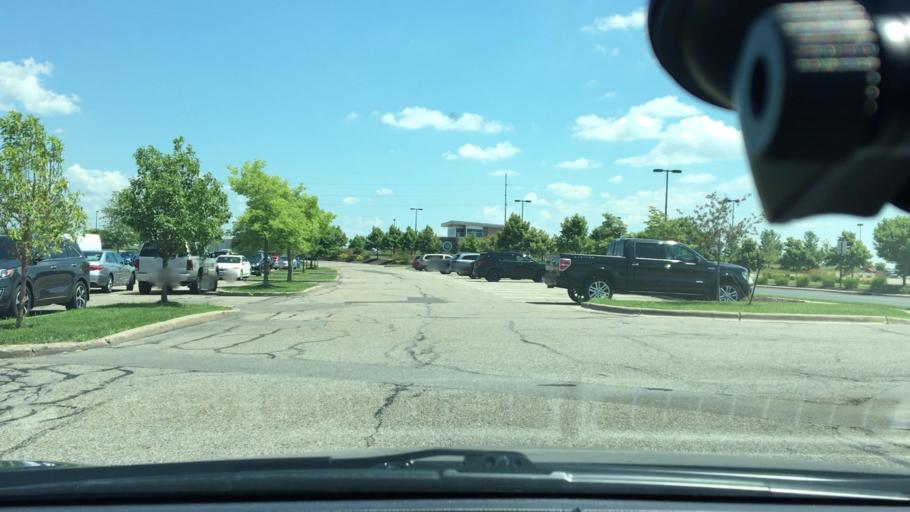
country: US
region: Minnesota
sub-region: Hennepin County
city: Osseo
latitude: 45.0918
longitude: -93.4245
